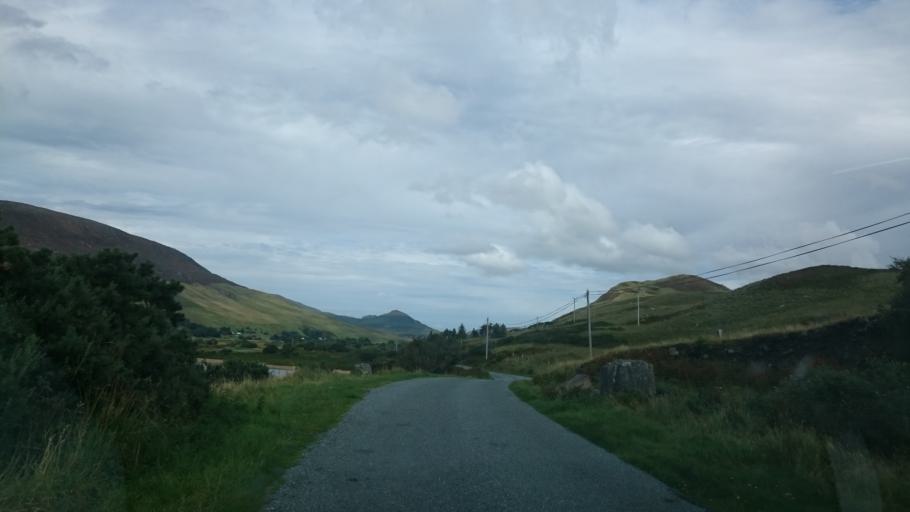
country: IE
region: Connaught
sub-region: Maigh Eo
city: Westport
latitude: 53.9547
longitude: -9.5696
